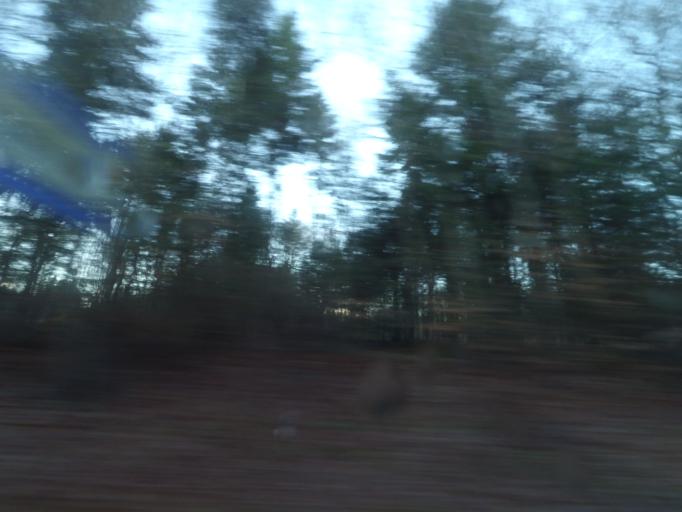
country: DK
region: Central Jutland
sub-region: Ikast-Brande Kommune
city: Brande
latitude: 56.0092
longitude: 9.0709
